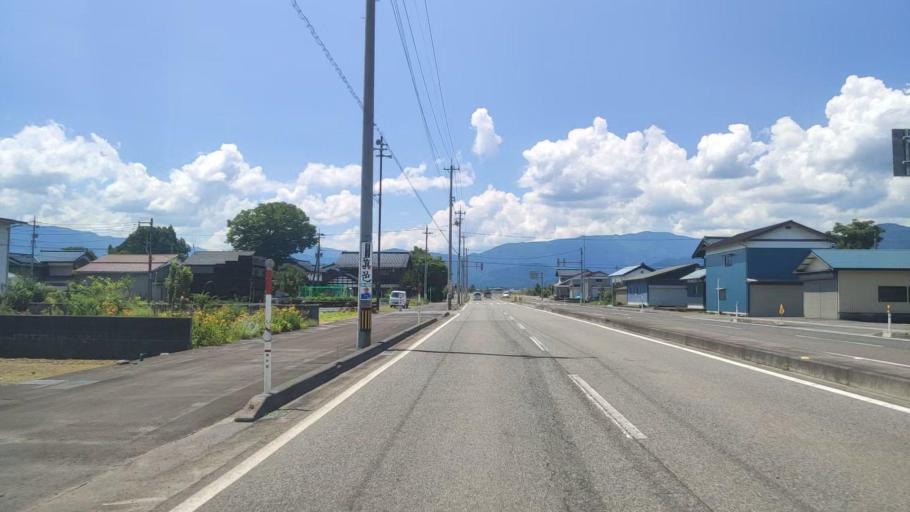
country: JP
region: Fukui
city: Ono
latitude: 36.0031
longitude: 136.5090
